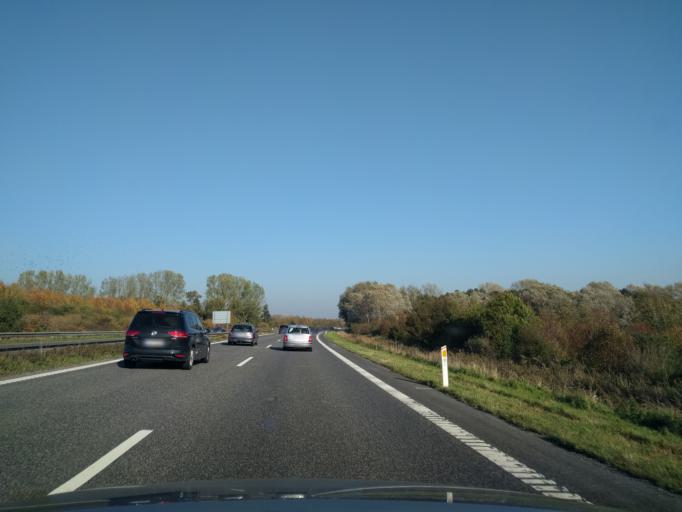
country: DK
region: Zealand
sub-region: Slagelse Kommune
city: Korsor
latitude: 55.3581
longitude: 11.1588
